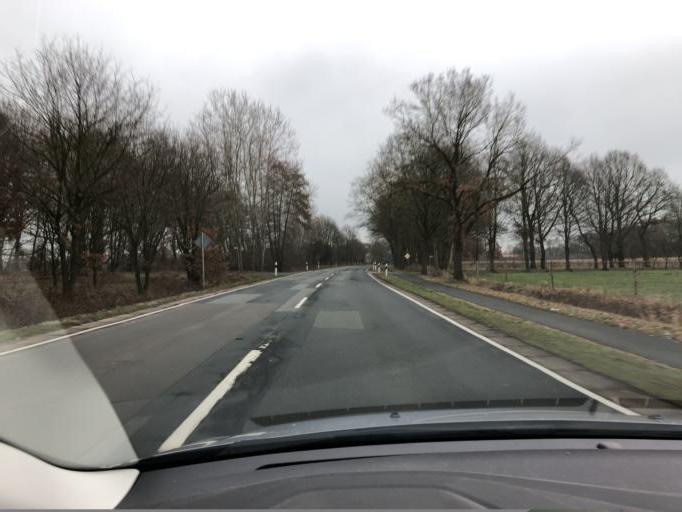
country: DE
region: Lower Saxony
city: Hatten
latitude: 53.0847
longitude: 8.3831
